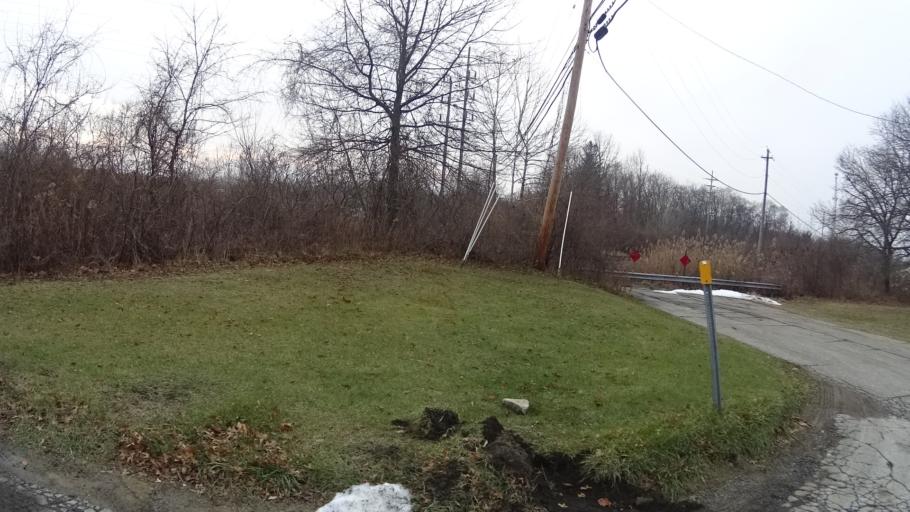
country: US
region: Ohio
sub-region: Lorain County
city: Amherst
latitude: 41.3907
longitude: -82.1995
